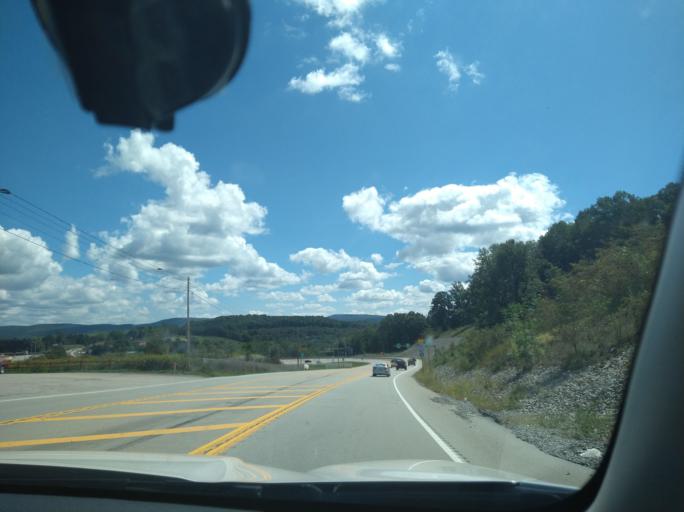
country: US
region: Pennsylvania
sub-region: Fayette County
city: Bear Rocks
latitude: 40.1098
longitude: -79.3848
